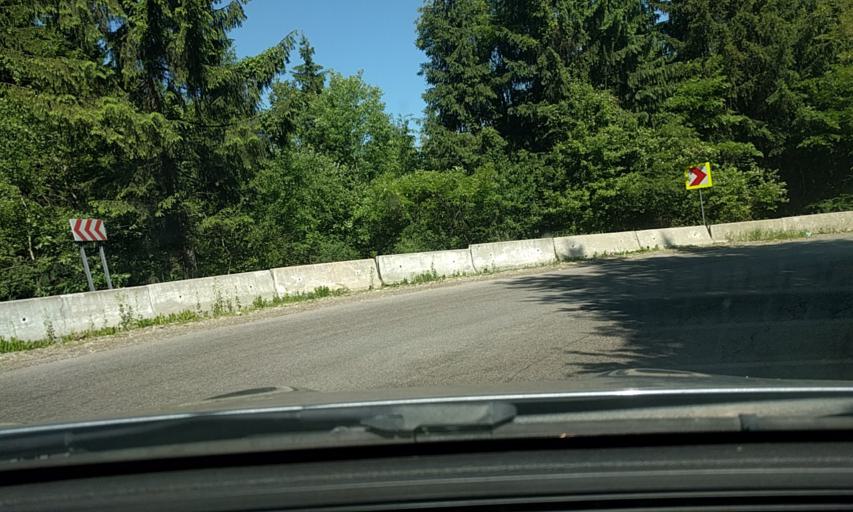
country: RO
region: Bistrita-Nasaud
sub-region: Comuna Dumitra
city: Dumitra
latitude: 47.1899
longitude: 24.4797
